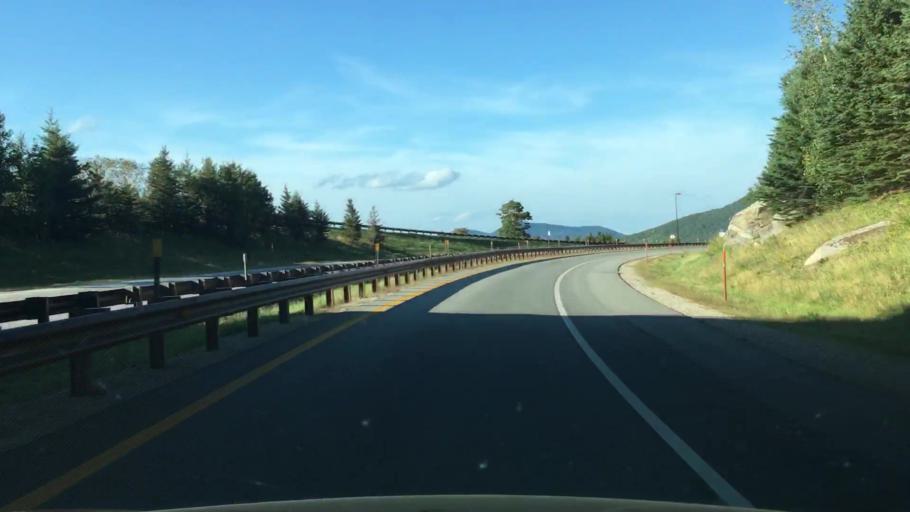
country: US
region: New Hampshire
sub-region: Grafton County
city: Deerfield
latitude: 44.1793
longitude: -71.6918
